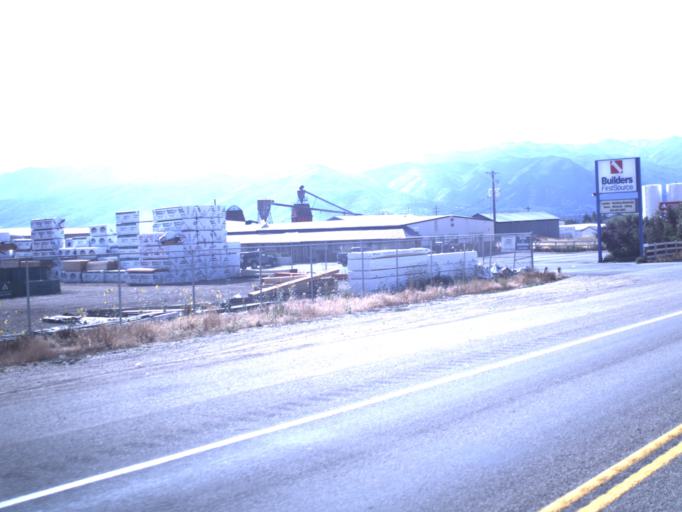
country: US
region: Utah
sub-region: Wasatch County
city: Heber
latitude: 40.4864
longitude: -111.4066
